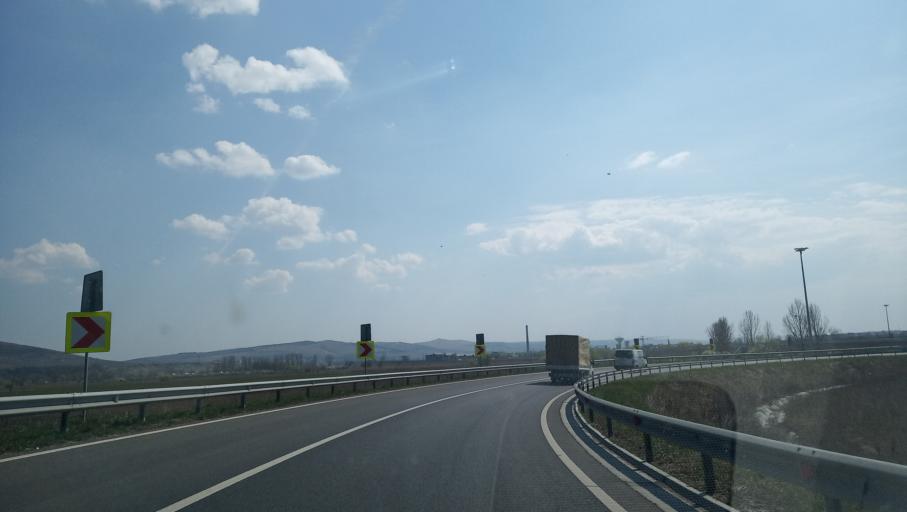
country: RO
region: Alba
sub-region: Municipiul Aiud
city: Aiud
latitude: 46.3291
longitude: 23.7325
